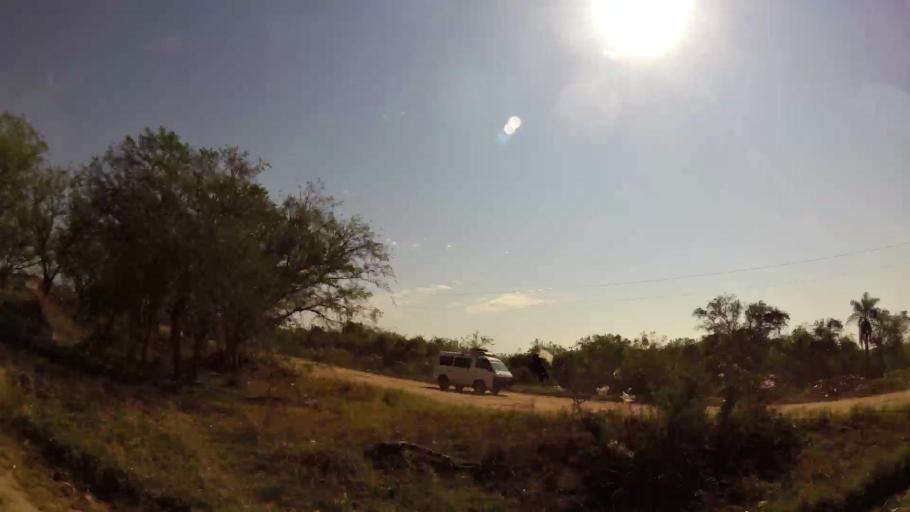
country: BO
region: Santa Cruz
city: Cotoca
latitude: -17.7107
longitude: -63.0624
